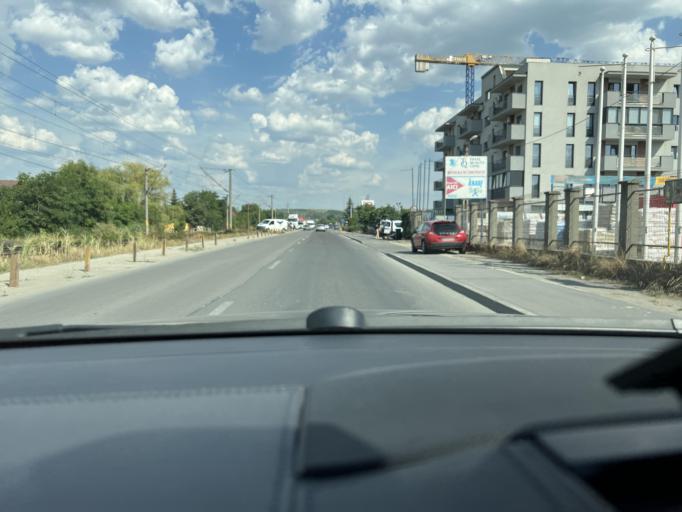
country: RO
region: Cluj
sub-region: Municipiul Cluj-Napoca
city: Cluj-Napoca
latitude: 46.7807
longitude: 23.6443
